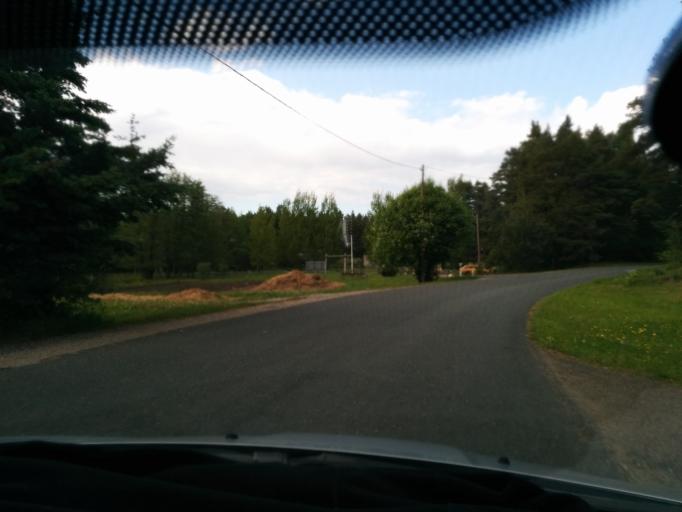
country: EE
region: Harju
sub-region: Loksa linn
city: Loksa
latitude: 59.6408
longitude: 25.6945
